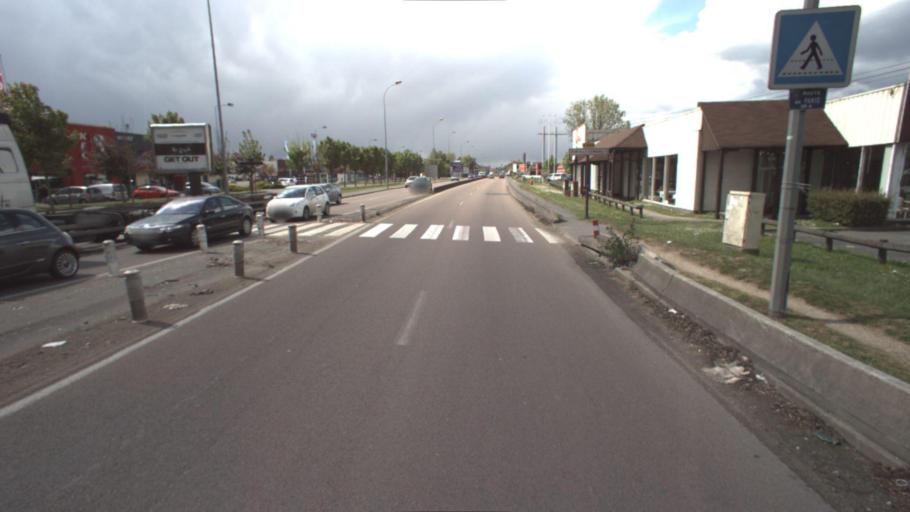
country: FR
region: Ile-de-France
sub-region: Departement de Seine-et-Marne
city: Pontault-Combault
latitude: 48.7757
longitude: 2.6026
